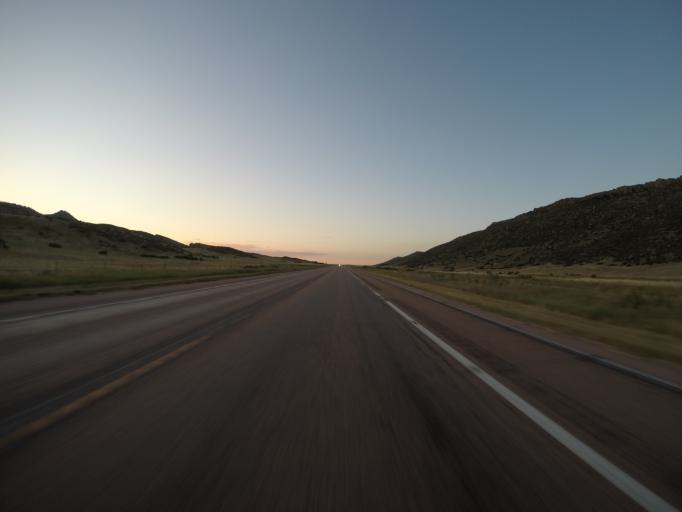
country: US
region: Colorado
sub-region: Larimer County
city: Laporte
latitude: 40.7169
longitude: -105.1722
